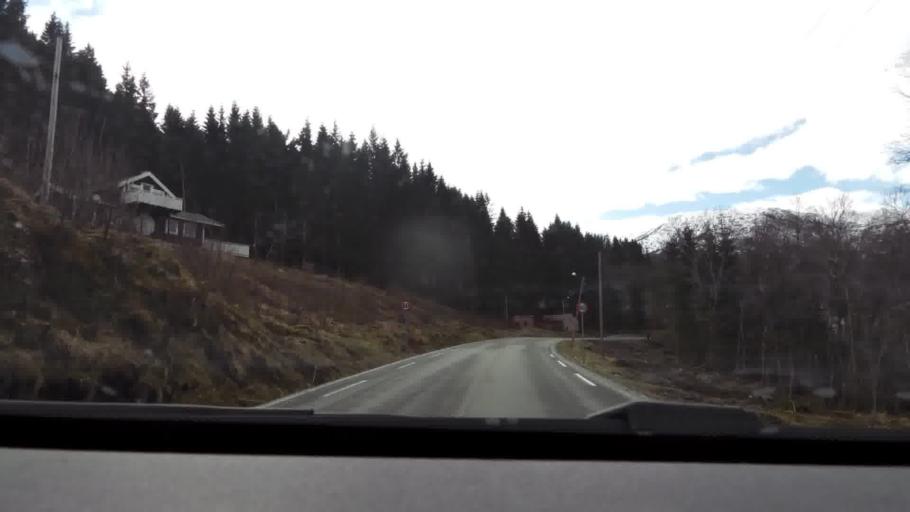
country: NO
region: More og Romsdal
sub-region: Eide
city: Eide
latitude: 62.9171
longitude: 7.5496
